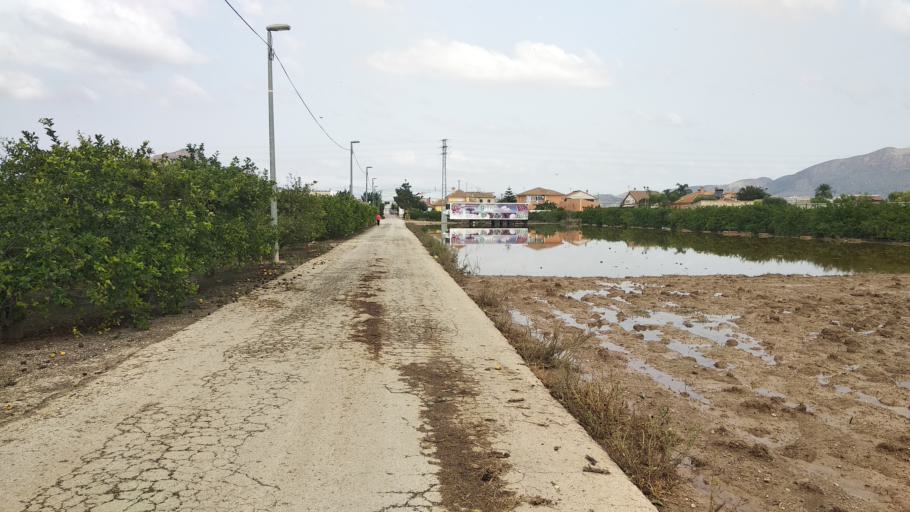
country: ES
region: Murcia
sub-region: Murcia
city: Santomera
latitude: 38.0410
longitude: -1.0407
